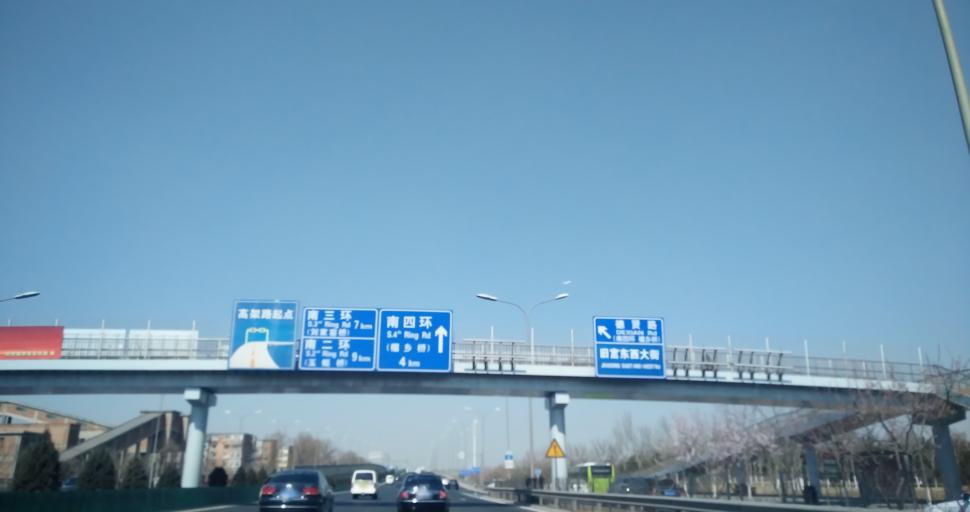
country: CN
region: Beijing
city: Jiugong
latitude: 39.7935
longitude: 116.4239
